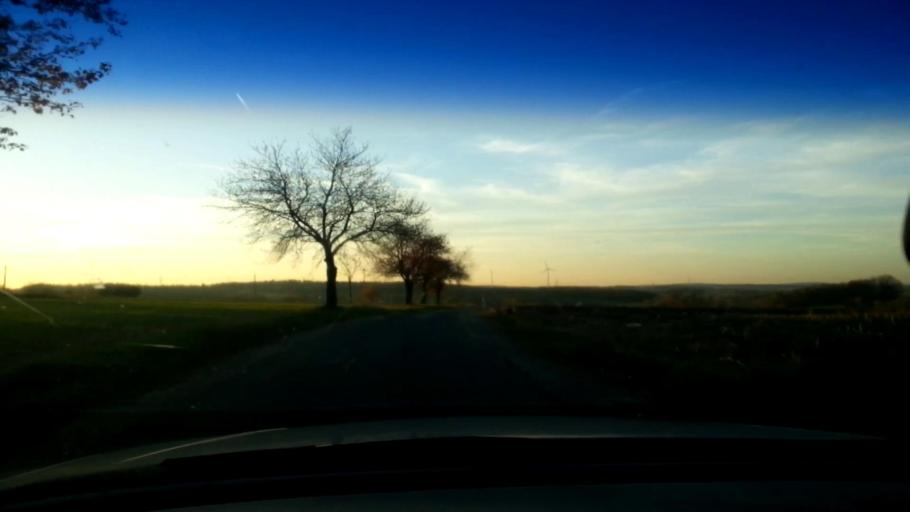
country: DE
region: Bavaria
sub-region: Upper Franconia
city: Heiligenstadt
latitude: 49.8424
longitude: 11.1290
